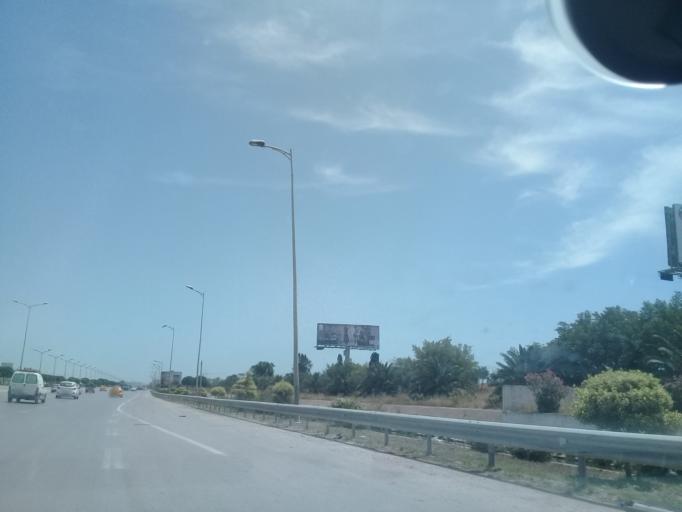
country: TN
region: Ariana
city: Ariana
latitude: 36.8332
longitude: 10.2171
